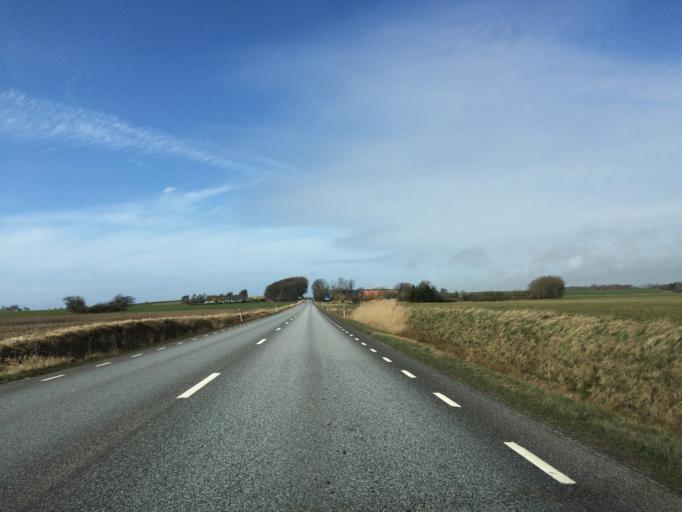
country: SE
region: Halland
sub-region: Halmstads Kommun
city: Paarp
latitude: 56.5842
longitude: 12.9961
